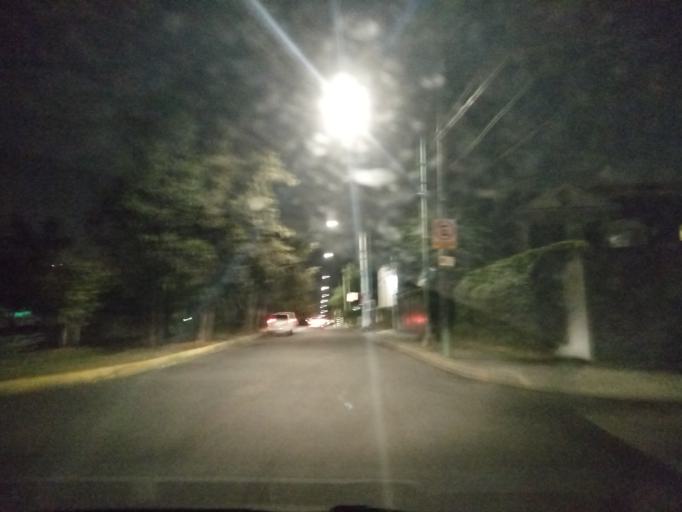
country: MX
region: Mexico City
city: Magdalena Contreras
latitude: 19.3090
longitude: -99.2023
